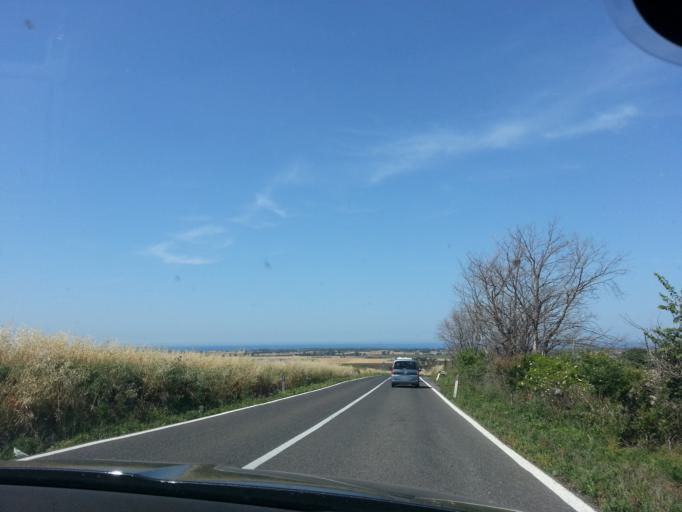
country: IT
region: Latium
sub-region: Provincia di Viterbo
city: Tarquinia
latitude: 42.2240
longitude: 11.7907
